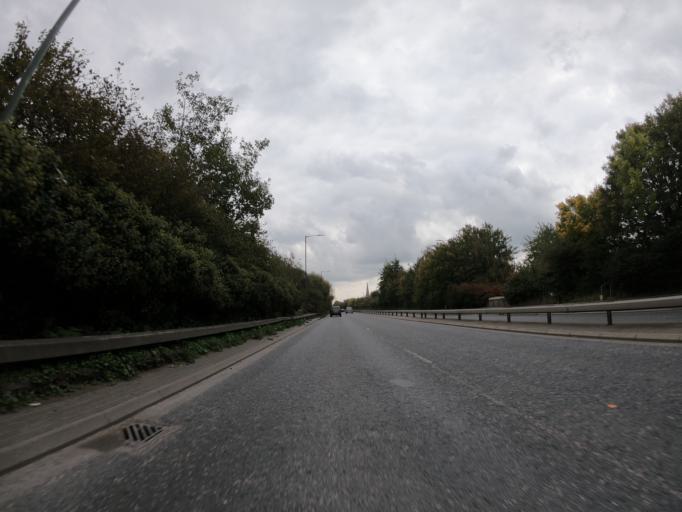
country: GB
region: England
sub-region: Greater London
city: Erith
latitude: 51.4845
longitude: 0.1720
